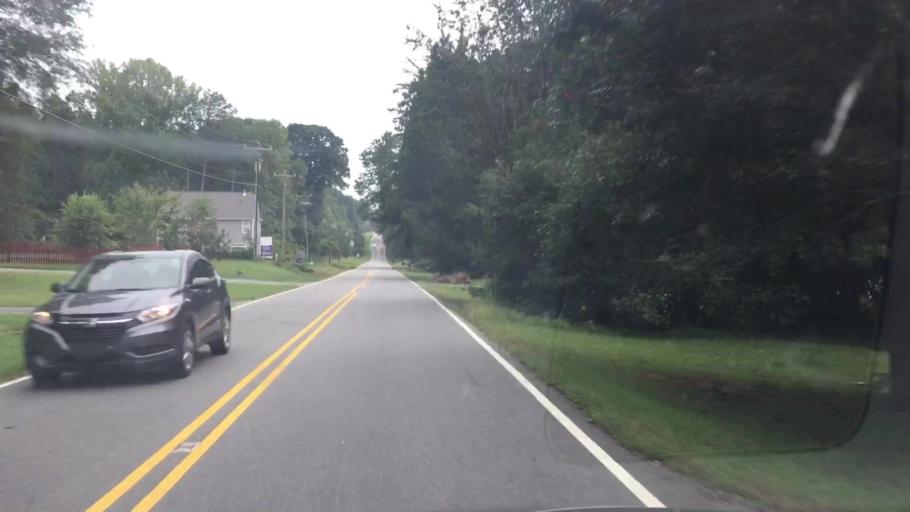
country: US
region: North Carolina
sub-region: Iredell County
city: Mooresville
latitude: 35.6071
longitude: -80.7930
